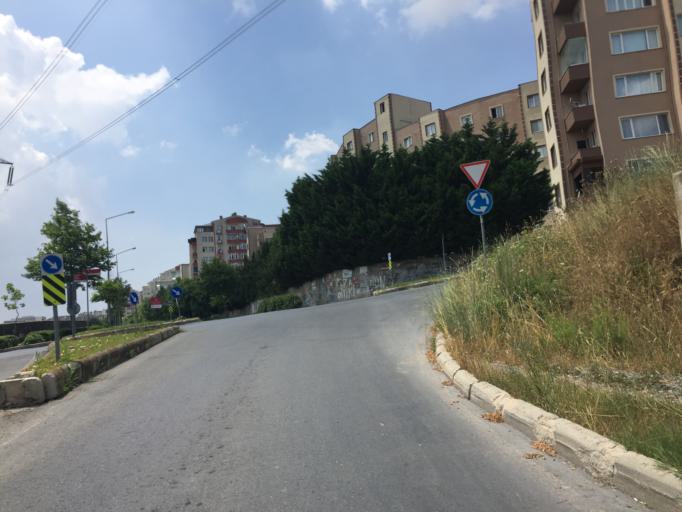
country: TR
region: Istanbul
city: Esenyurt
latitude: 41.0759
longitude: 28.6693
